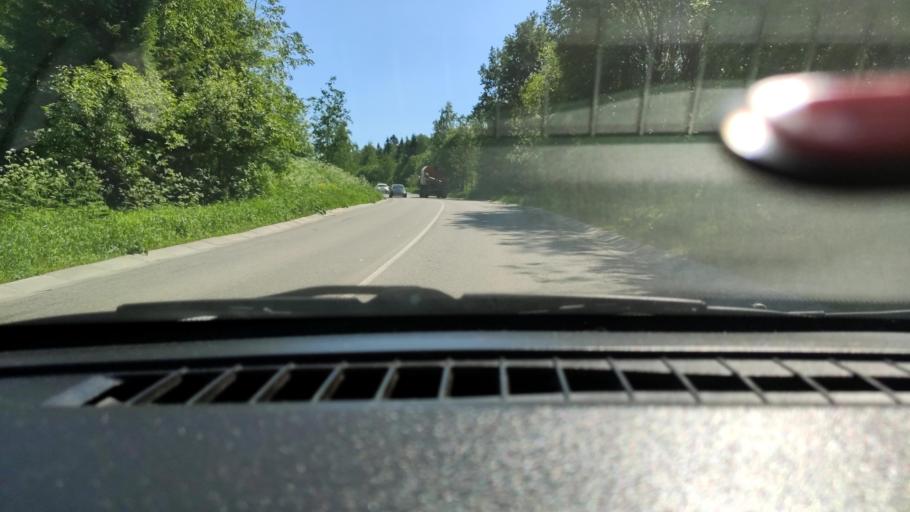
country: RU
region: Perm
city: Novyye Lyady
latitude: 58.0369
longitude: 56.6006
